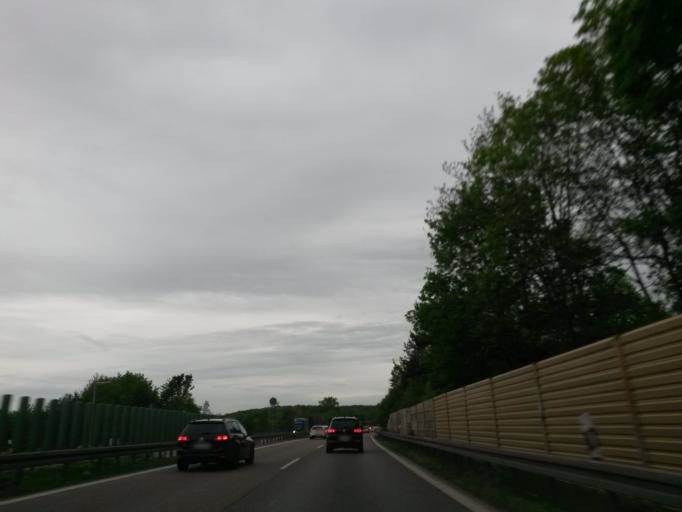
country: DE
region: Baden-Wuerttemberg
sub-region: Regierungsbezirk Stuttgart
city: Stuttgart Feuerbach
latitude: 48.8407
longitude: 9.1584
